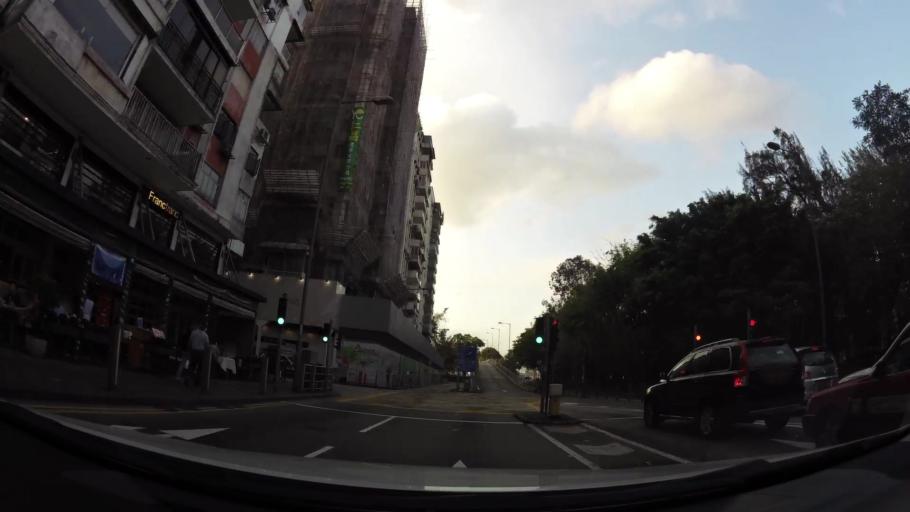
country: HK
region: Wanchai
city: Wan Chai
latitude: 22.2817
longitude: 114.1866
